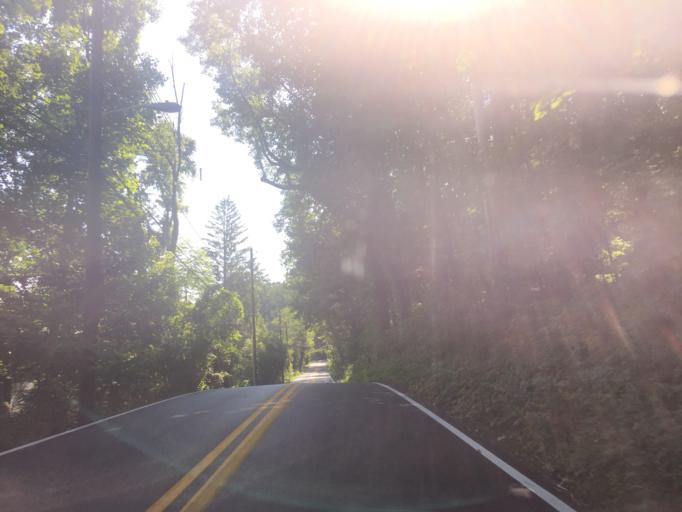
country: US
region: Maryland
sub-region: Baltimore County
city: Pikesville
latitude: 39.4124
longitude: -76.6964
